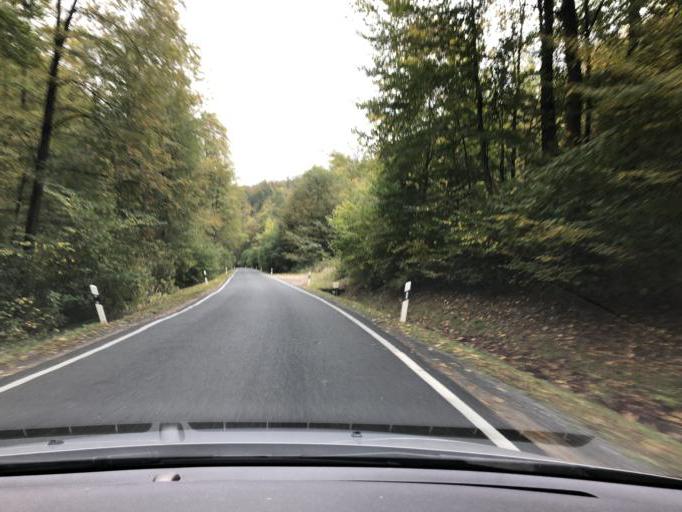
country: DE
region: Thuringia
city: Grossbartloff
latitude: 51.2634
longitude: 10.2253
